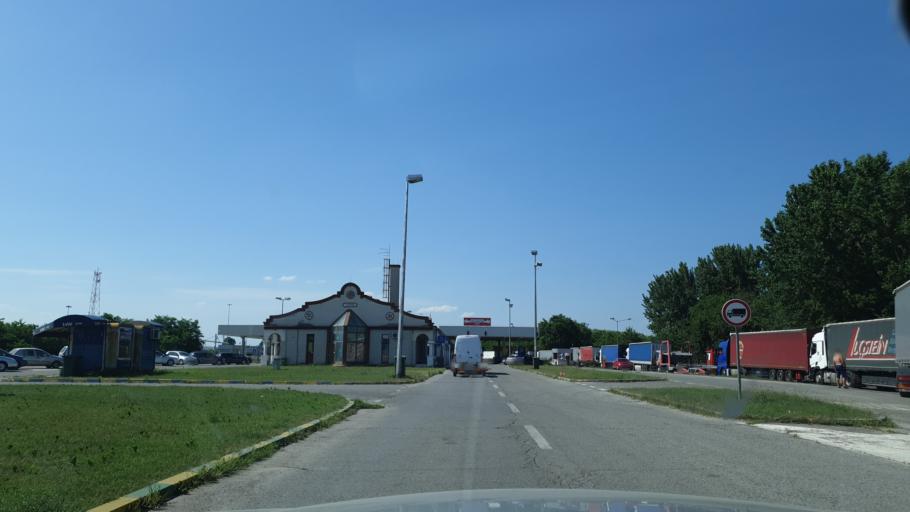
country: HU
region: Bacs-Kiskun
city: Tompa
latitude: 46.1660
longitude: 19.5624
